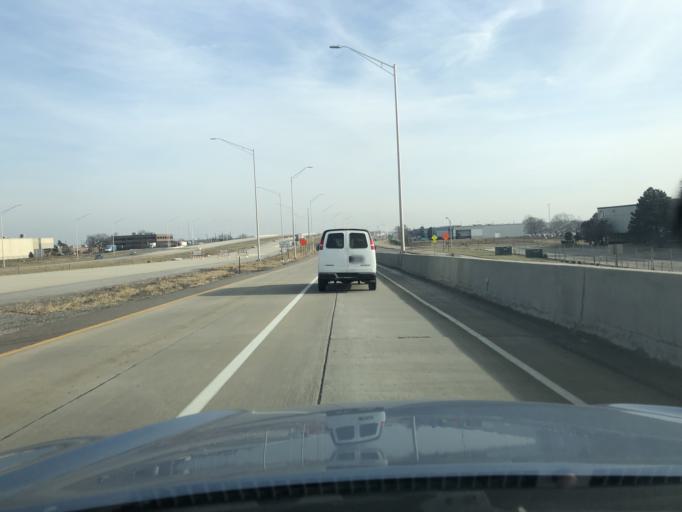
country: US
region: Illinois
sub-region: Cook County
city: Elk Grove Village
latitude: 41.9829
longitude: -87.9663
